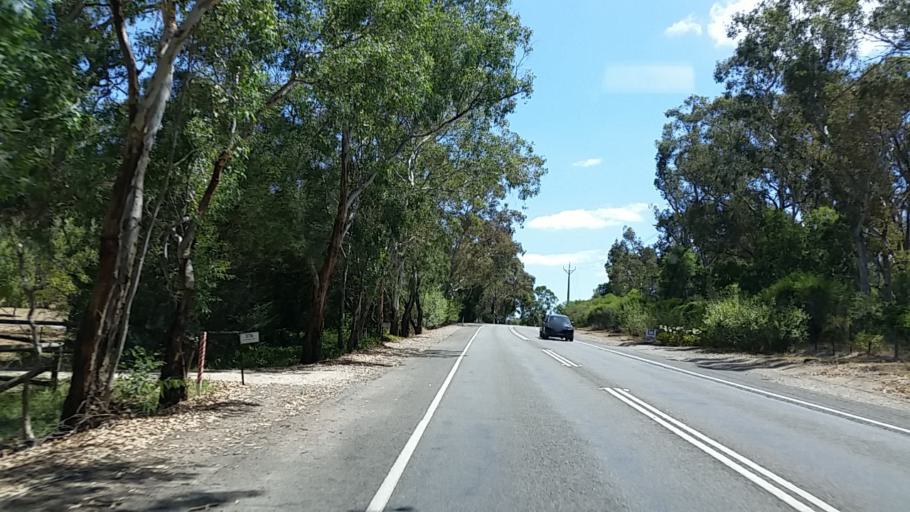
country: AU
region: South Australia
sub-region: Mount Barker
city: Nairne
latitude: -35.0399
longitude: 138.8878
